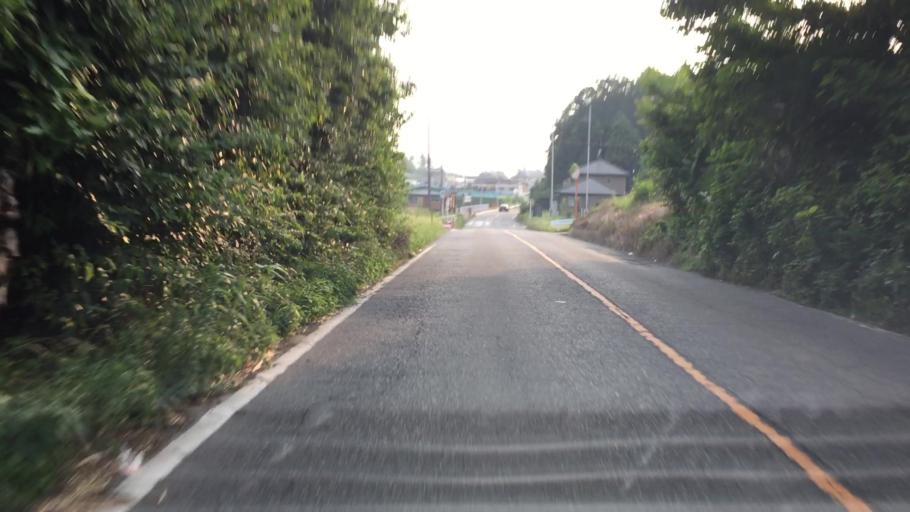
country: JP
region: Tochigi
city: Fujioka
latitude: 36.2610
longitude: 139.6265
